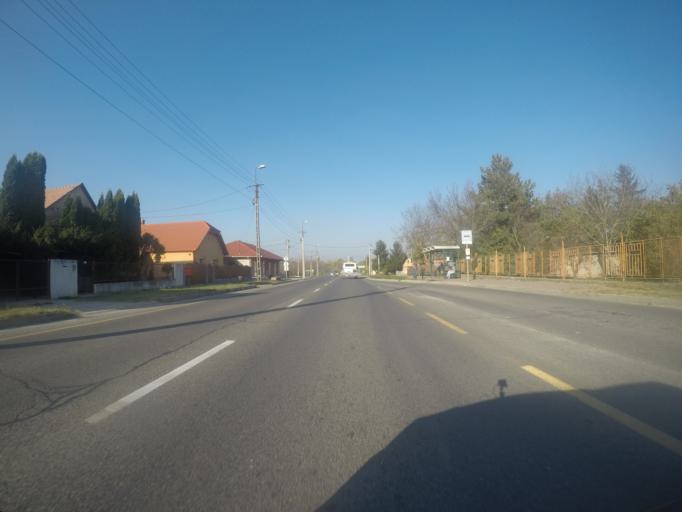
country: HU
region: Fejer
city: Ercsi
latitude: 47.2582
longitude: 18.8939
